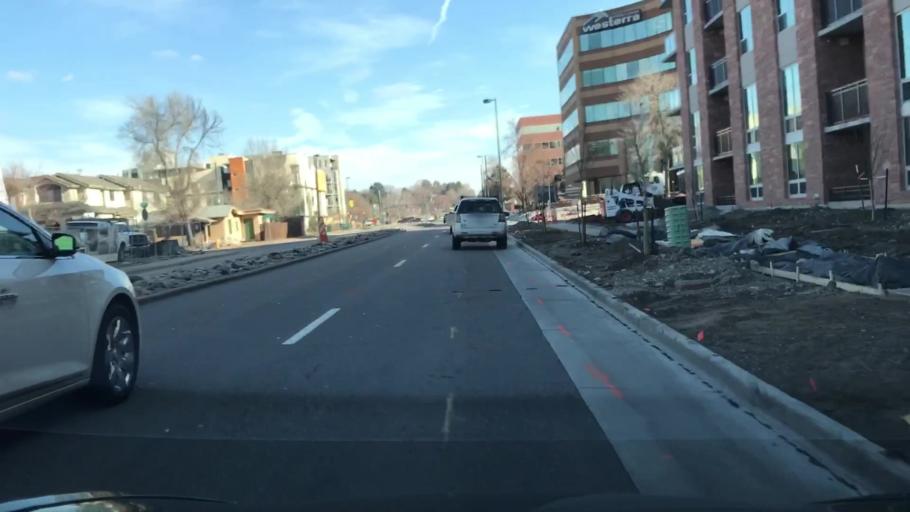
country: US
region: Colorado
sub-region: Arapahoe County
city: Glendale
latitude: 39.7114
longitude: -104.9444
